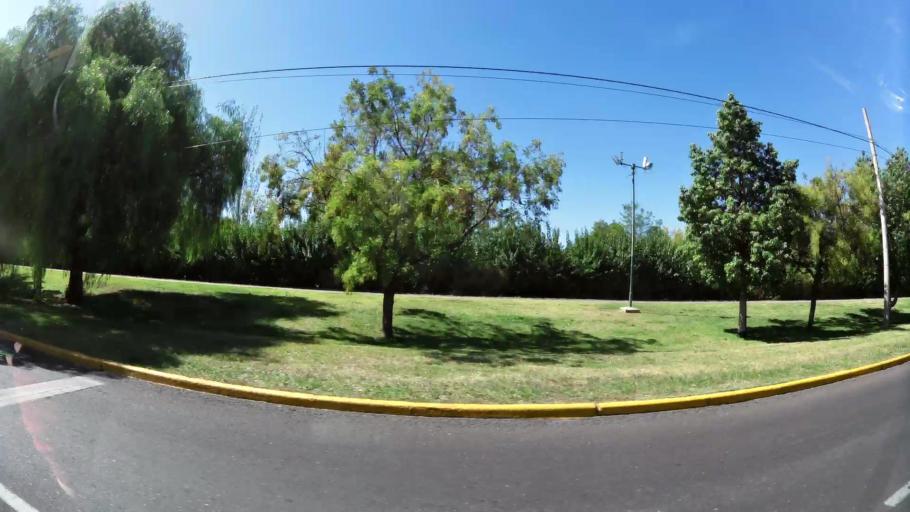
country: AR
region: Mendoza
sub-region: Departamento de Godoy Cruz
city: Godoy Cruz
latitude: -32.9471
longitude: -68.8528
